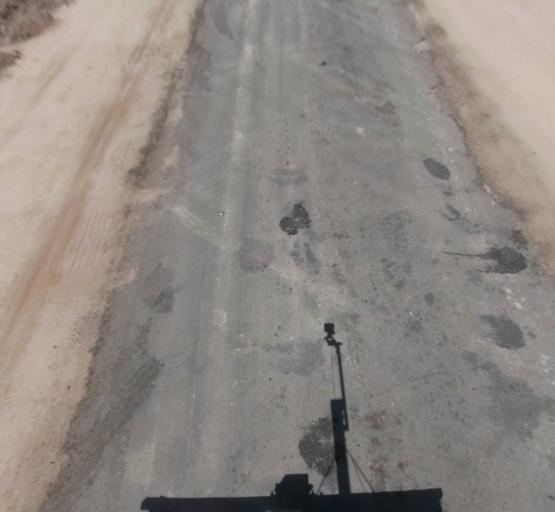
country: US
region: California
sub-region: Madera County
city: Fairmead
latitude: 37.0161
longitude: -120.1842
